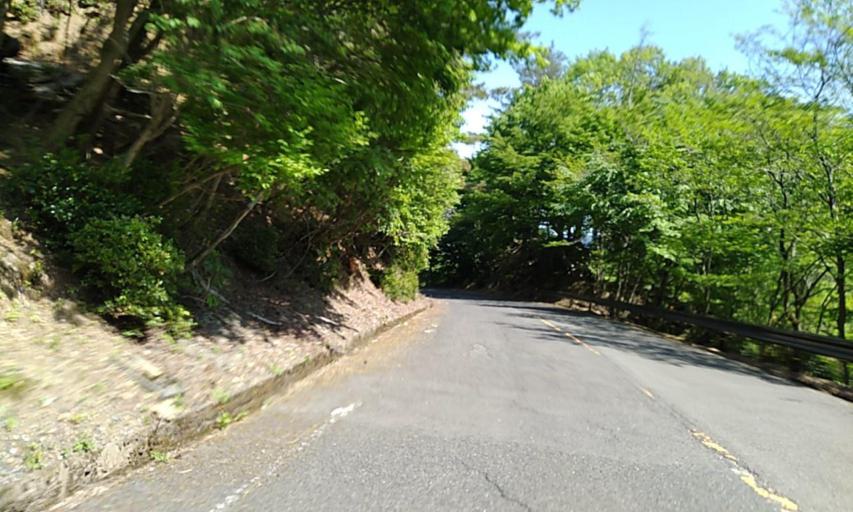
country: JP
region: Fukui
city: Obama
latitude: 35.5501
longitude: 135.7414
